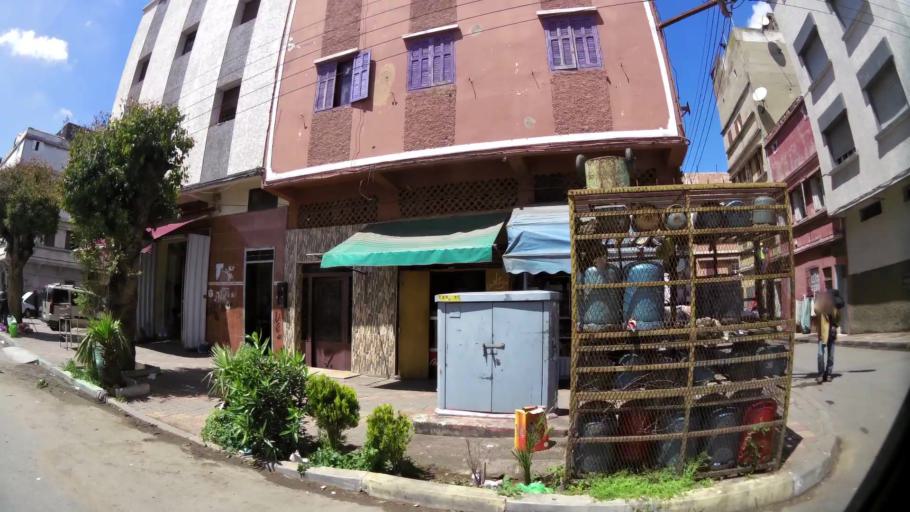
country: MA
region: Grand Casablanca
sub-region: Casablanca
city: Casablanca
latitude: 33.5651
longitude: -7.5728
